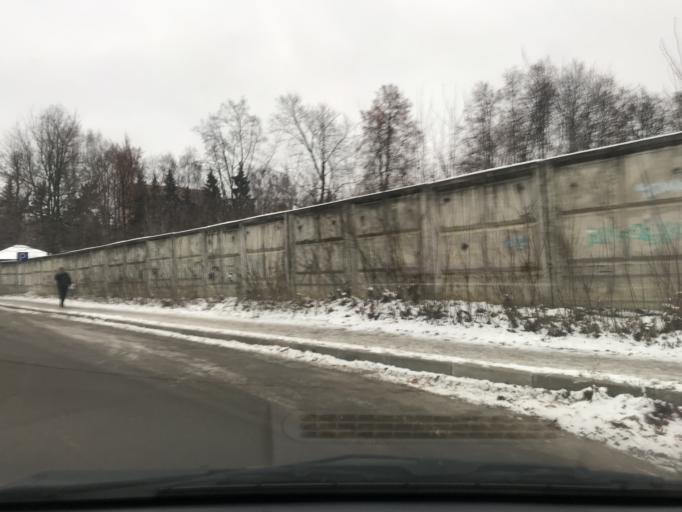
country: RU
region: Moskovskaya
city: Elektrostal'
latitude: 55.8037
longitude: 38.4653
